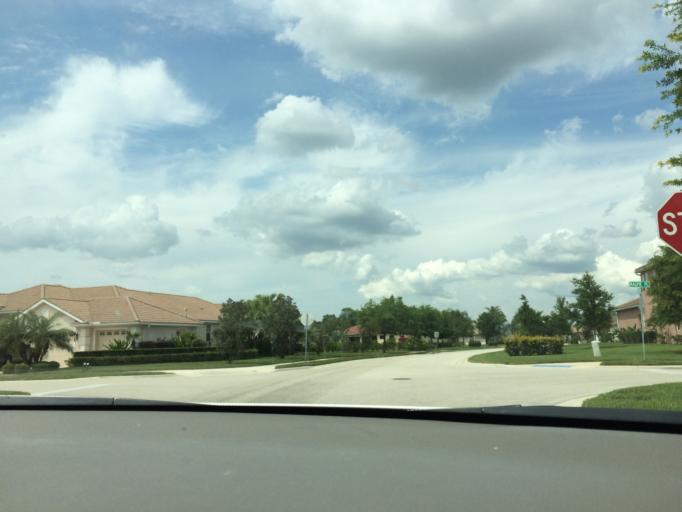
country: US
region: Florida
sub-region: Manatee County
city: Ellenton
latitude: 27.4981
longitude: -82.4126
